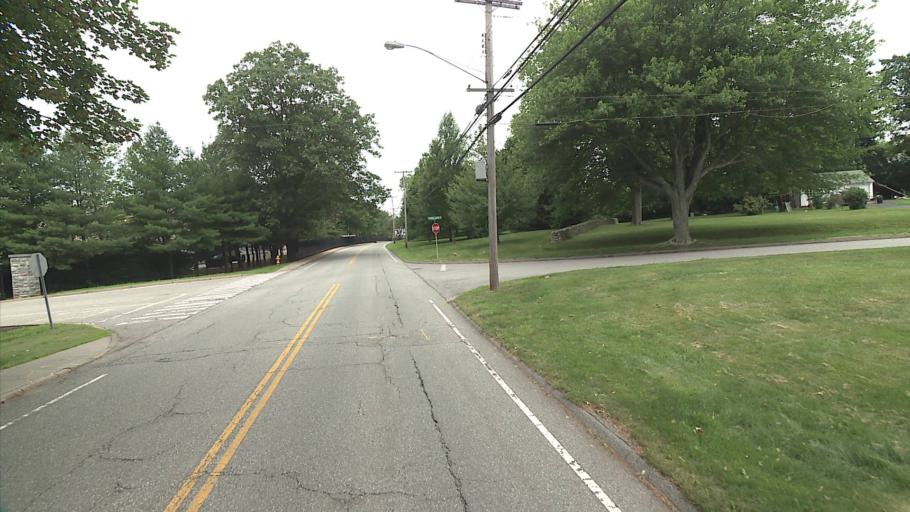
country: US
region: Connecticut
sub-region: New London County
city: Groton
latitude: 41.3283
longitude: -72.0742
